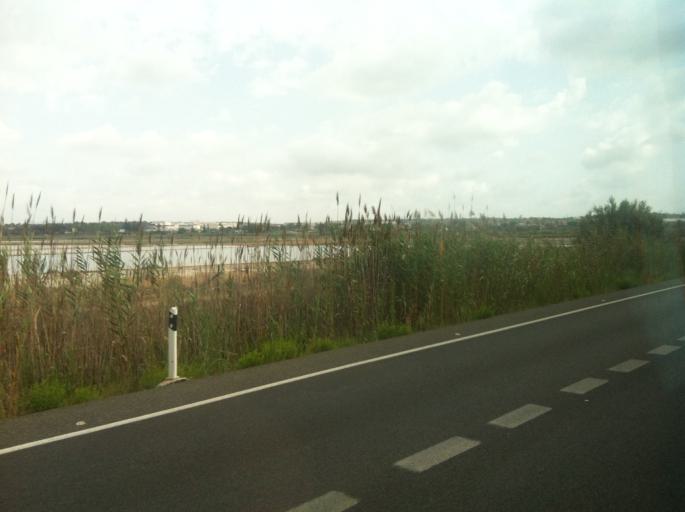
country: ES
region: Valencia
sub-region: Provincia de Alicante
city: Santa Pola
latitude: 38.1960
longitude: -0.5818
